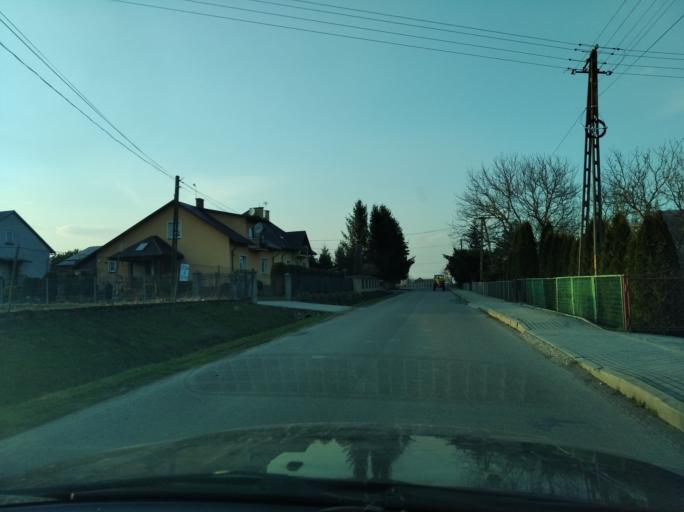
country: PL
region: Subcarpathian Voivodeship
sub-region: Powiat przeworski
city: Zarzecze
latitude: 49.9656
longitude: 22.5572
